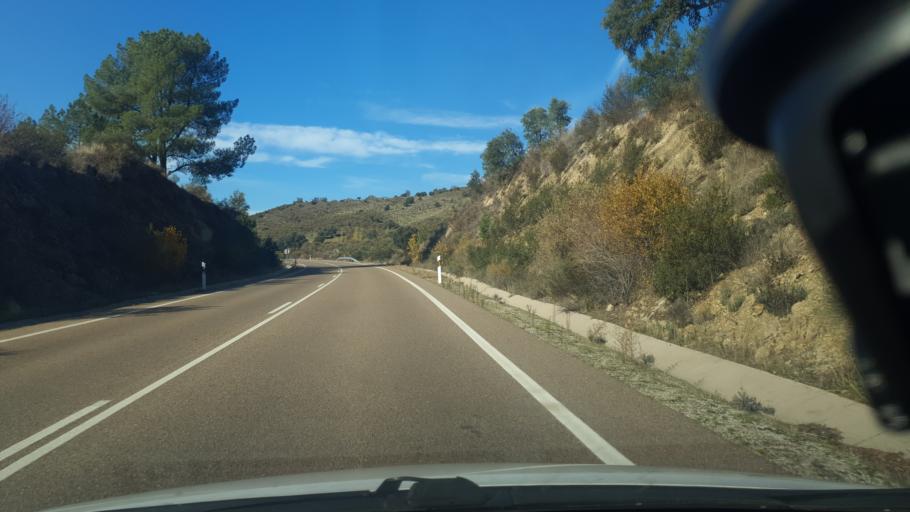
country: ES
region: Castille and Leon
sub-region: Provincia de Avila
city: Poyales del Hoyo
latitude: 40.1588
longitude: -5.1597
